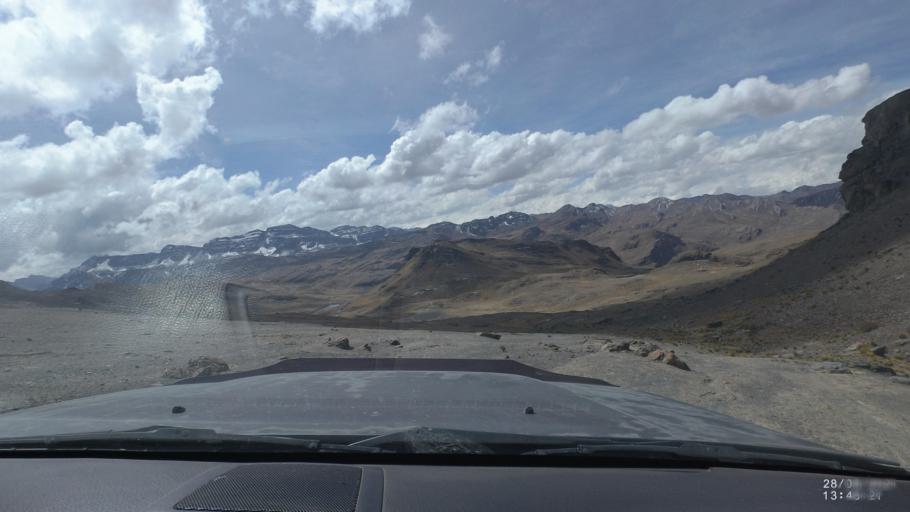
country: BO
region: Cochabamba
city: Sipe Sipe
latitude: -17.2811
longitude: -66.3817
